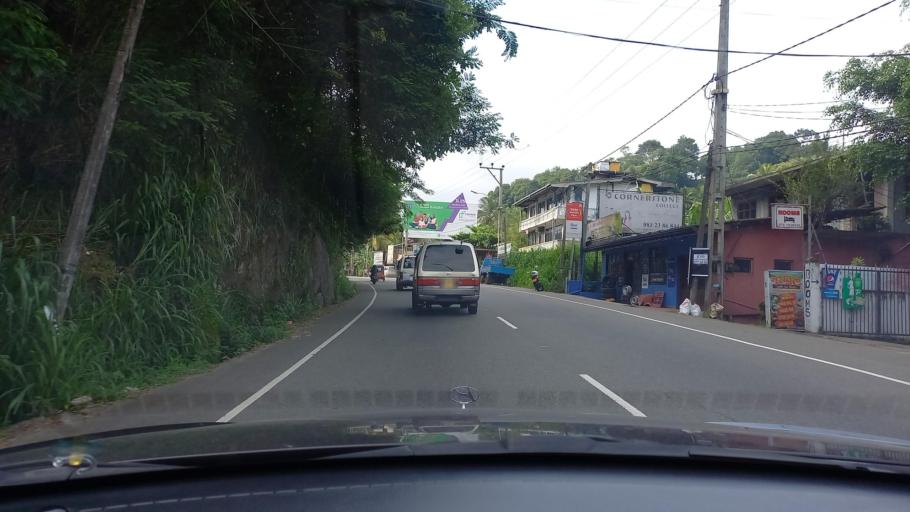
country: LK
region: Central
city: Kadugannawa
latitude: 7.2675
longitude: 80.5812
